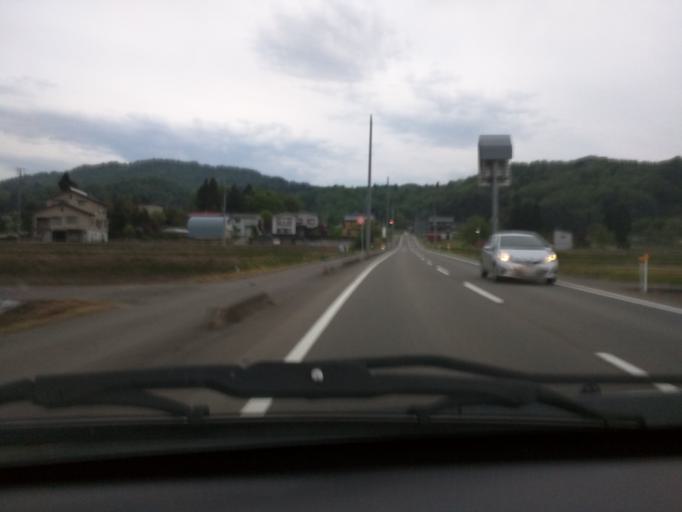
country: JP
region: Niigata
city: Ojiya
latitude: 37.3099
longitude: 138.7769
